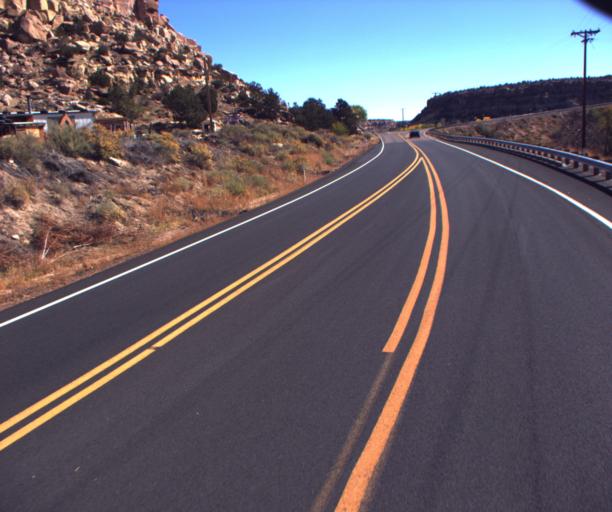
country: US
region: Arizona
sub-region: Navajo County
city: First Mesa
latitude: 35.8139
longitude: -110.2039
